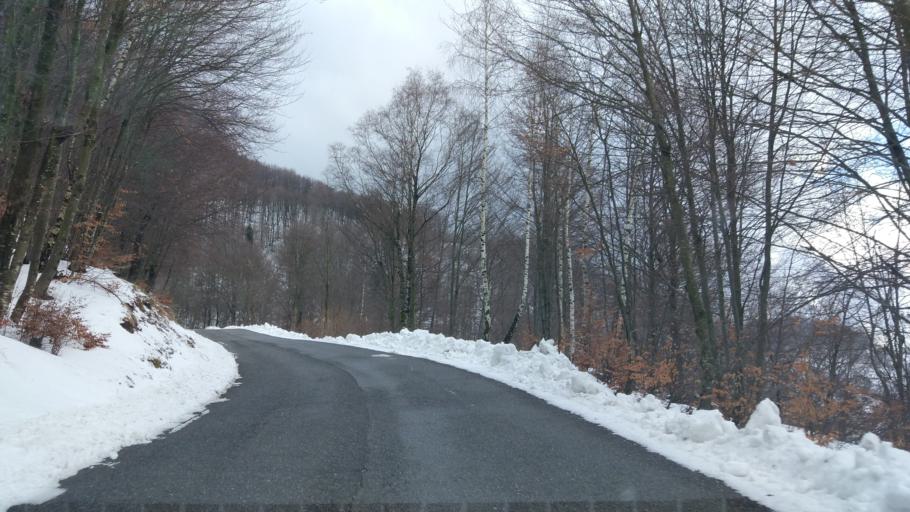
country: IT
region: Lombardy
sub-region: Provincia di Lecco
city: Moggio
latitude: 45.9085
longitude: 9.4978
